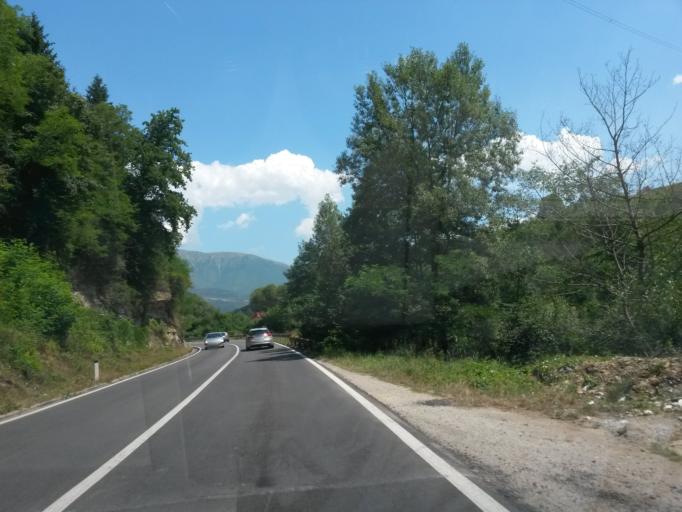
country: BA
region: Federation of Bosnia and Herzegovina
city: Turbe
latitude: 44.2349
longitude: 17.5660
